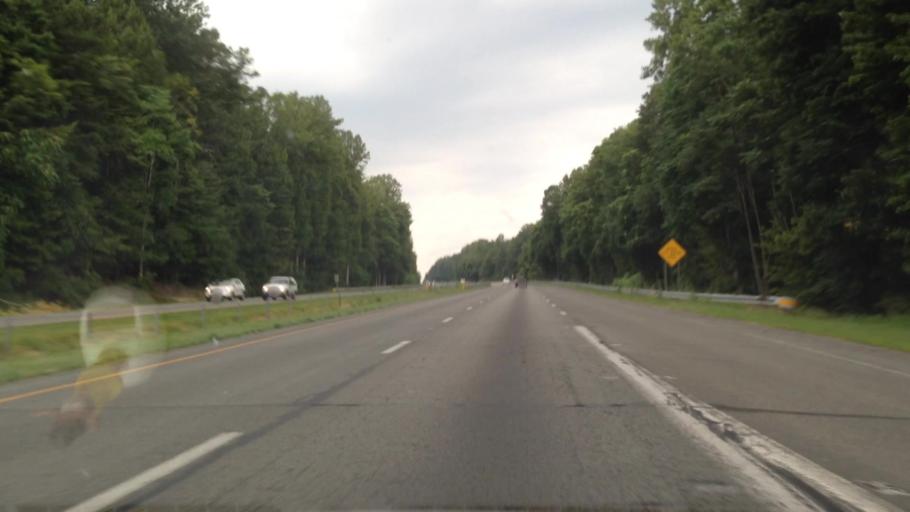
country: US
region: North Carolina
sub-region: Surry County
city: Pilot Mountain
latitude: 36.3395
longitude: -80.4577
